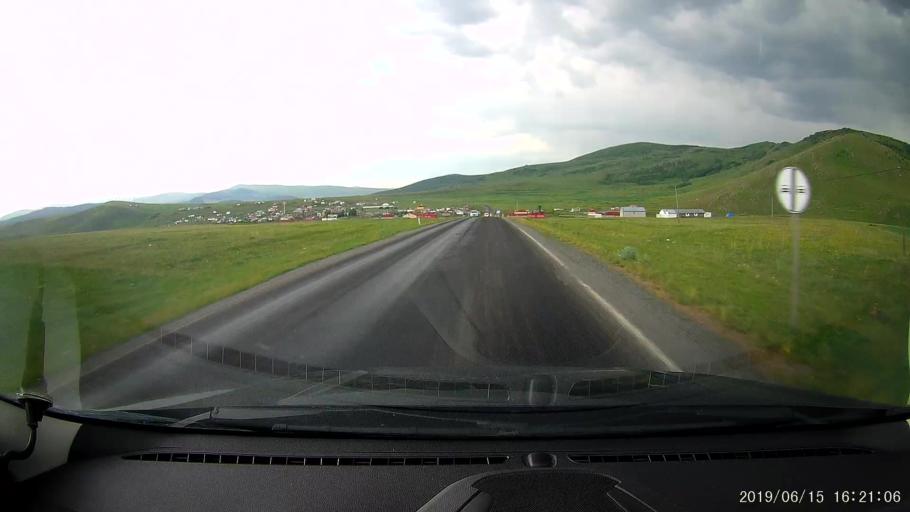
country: TR
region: Ardahan
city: Hanak
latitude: 41.2026
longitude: 42.8462
